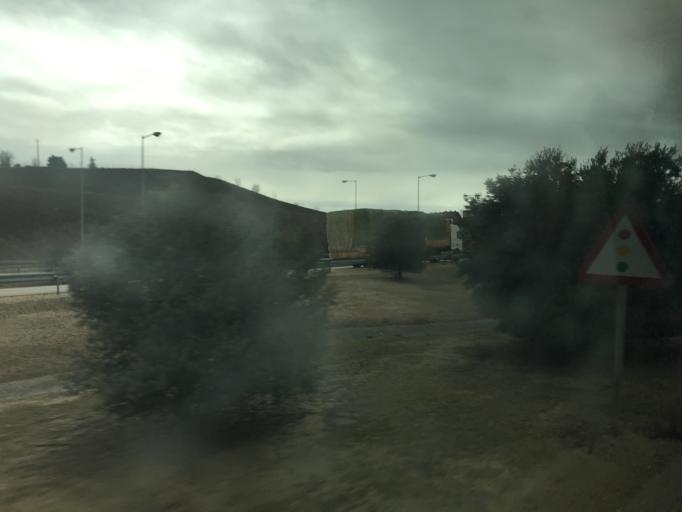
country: ES
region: Castille and Leon
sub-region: Provincia de Valladolid
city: Zaratan
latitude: 41.6563
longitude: -4.7642
